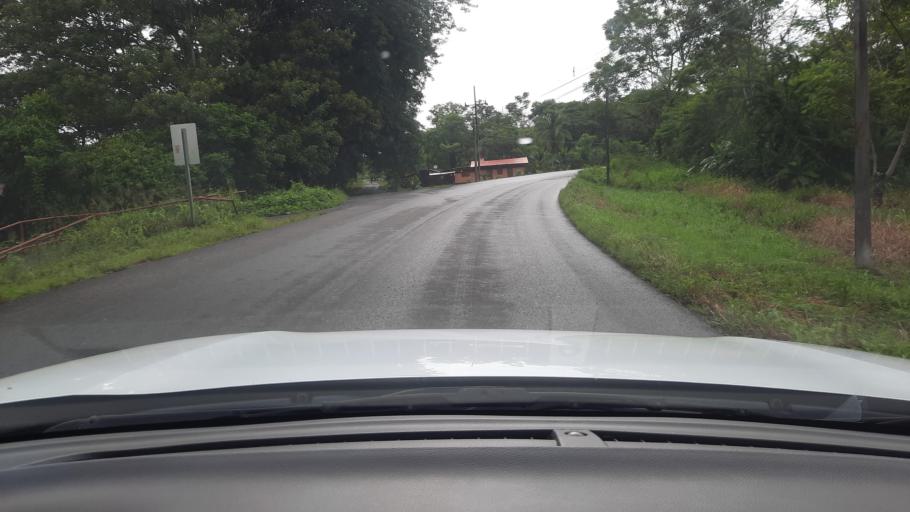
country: CR
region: Alajuela
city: San Jose
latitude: 10.9292
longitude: -85.0867
